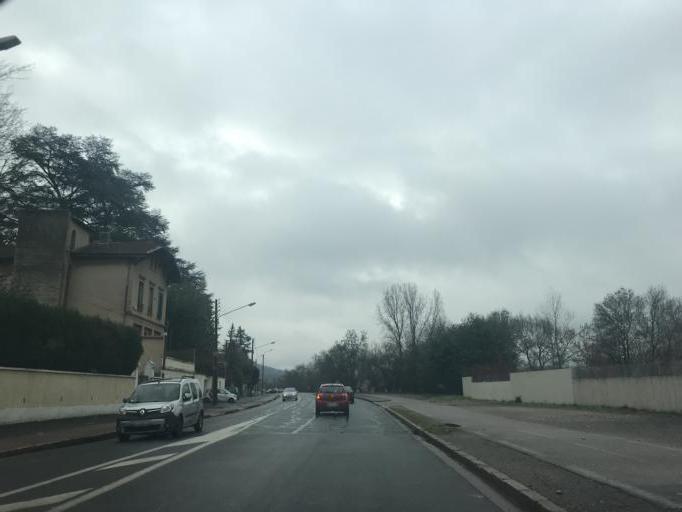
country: FR
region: Rhone-Alpes
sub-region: Departement du Rhone
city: Fleurieu-sur-Saone
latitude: 45.8675
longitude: 4.8395
